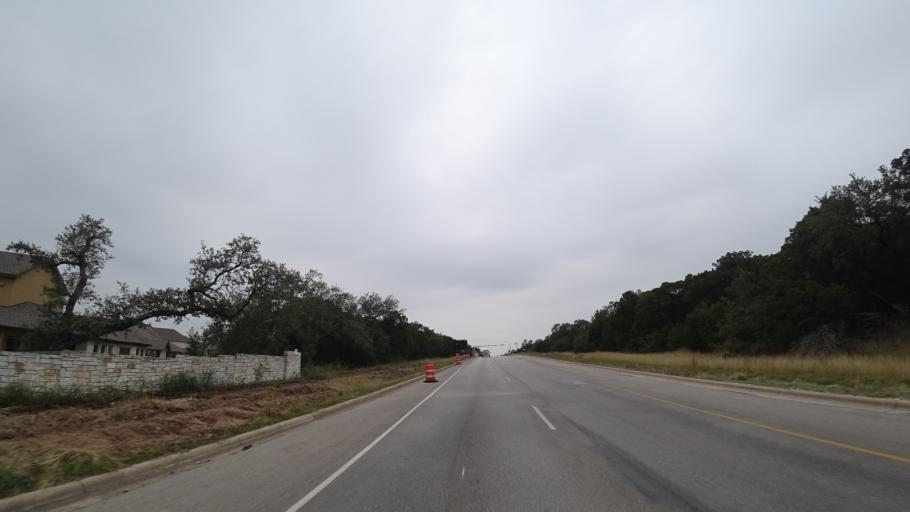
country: US
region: Texas
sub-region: Travis County
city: Shady Hollow
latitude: 30.1804
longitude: -97.8988
